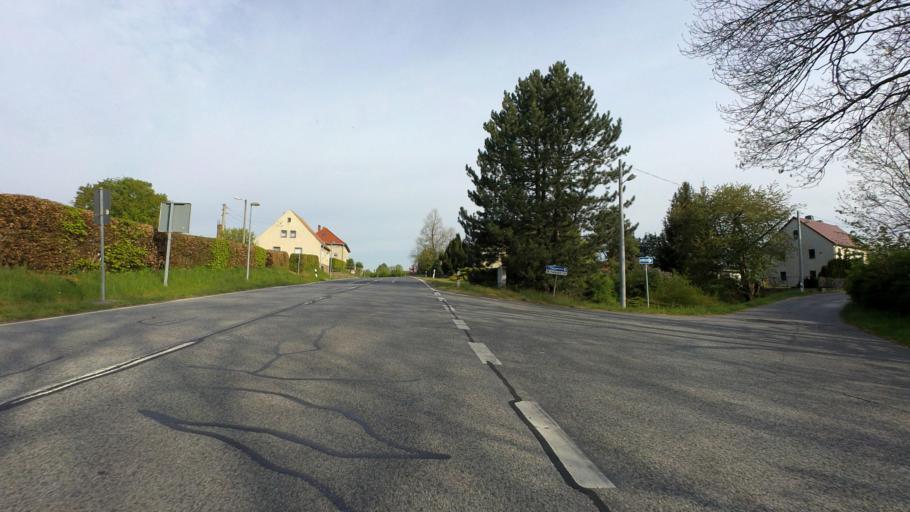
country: DE
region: Saxony
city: Stolpen
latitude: 51.0570
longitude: 14.0634
